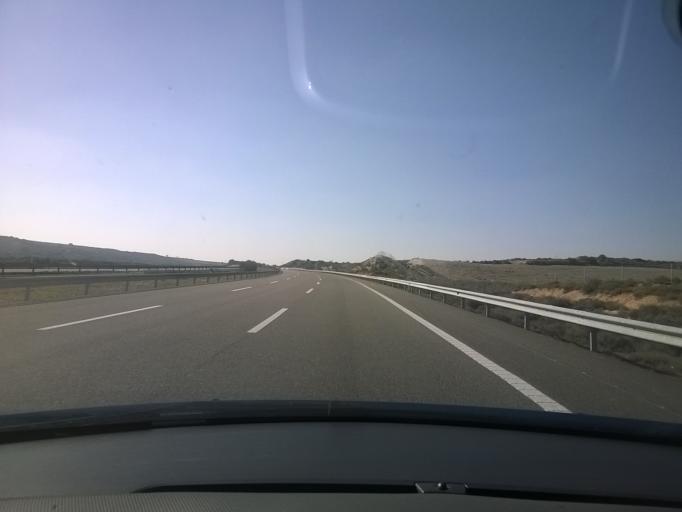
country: ES
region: Aragon
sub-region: Provincia de Huesca
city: Penalba
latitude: 41.5147
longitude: -0.0570
